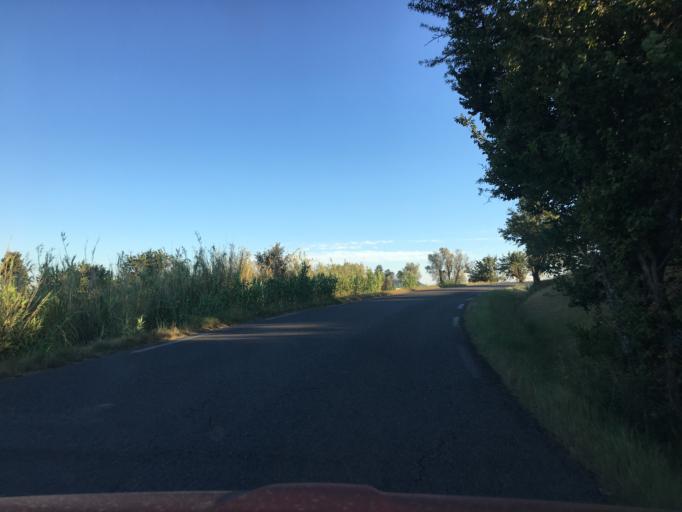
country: FR
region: Provence-Alpes-Cote d'Azur
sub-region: Departement des Bouches-du-Rhone
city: Noves
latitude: 43.8407
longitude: 4.8872
